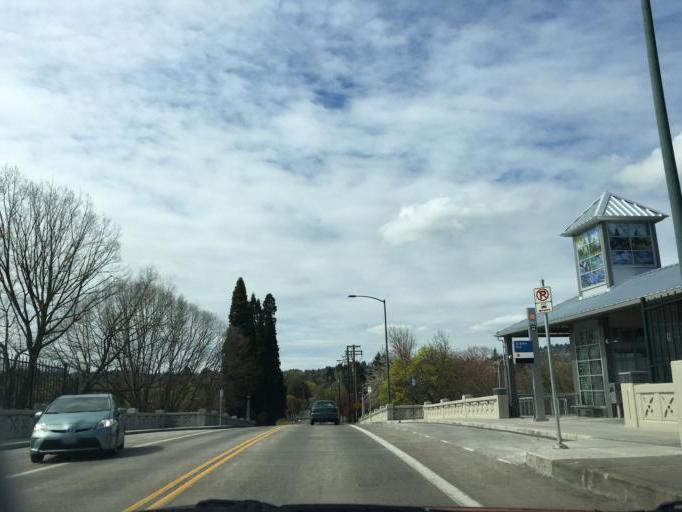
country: US
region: Oregon
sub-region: Clackamas County
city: Milwaukie
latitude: 45.4743
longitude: -122.6396
